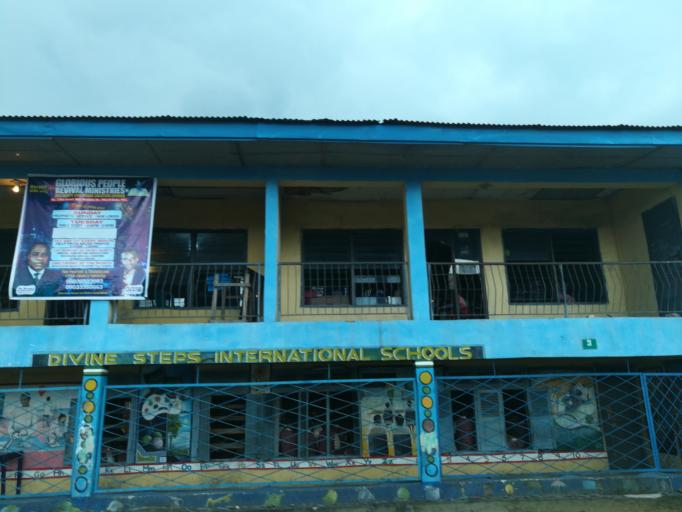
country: NG
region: Rivers
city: Port Harcourt
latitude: 4.7971
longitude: 6.9875
